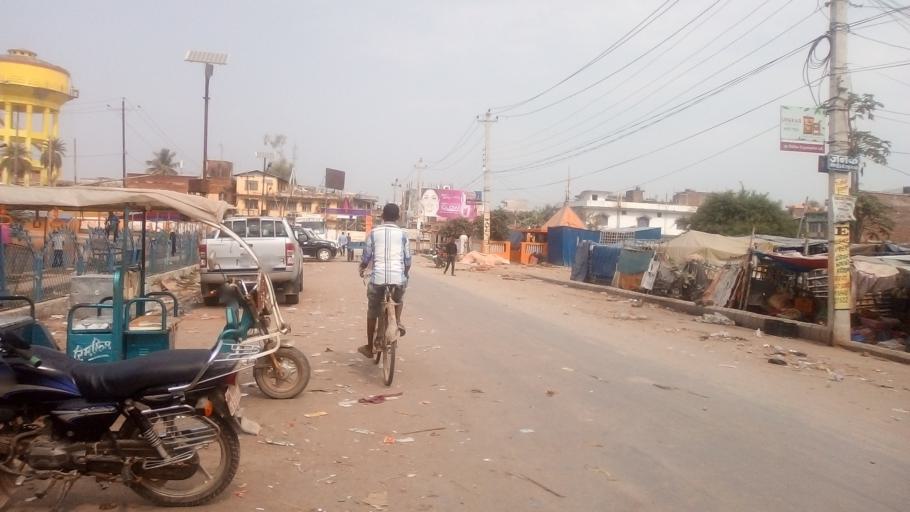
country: NP
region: Central Region
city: Janakpur
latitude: 26.7316
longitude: 85.9259
